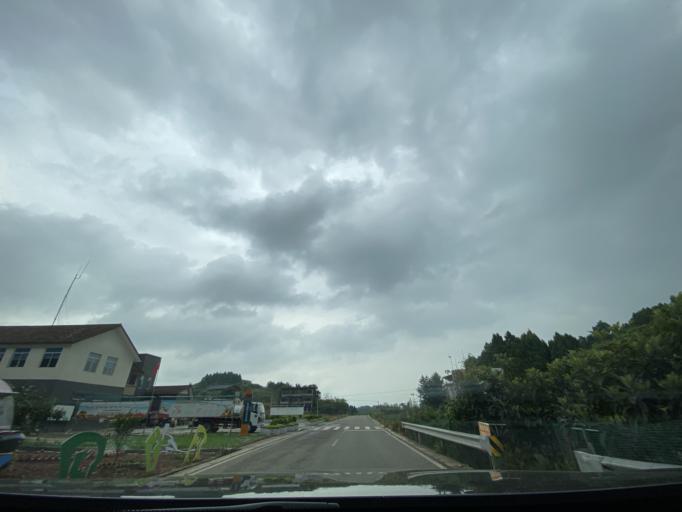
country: CN
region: Sichuan
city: Jiancheng
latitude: 30.5339
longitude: 104.5359
